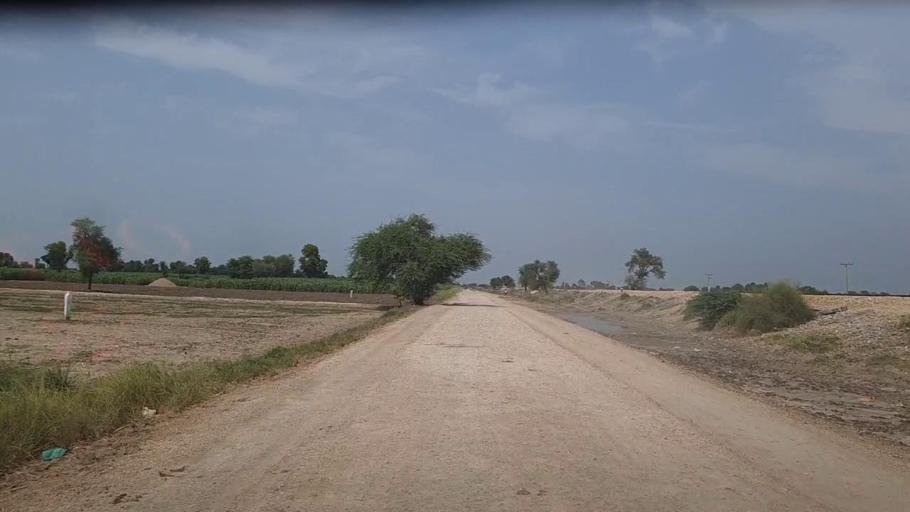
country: PK
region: Sindh
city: Bhiria
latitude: 26.9052
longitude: 68.2906
